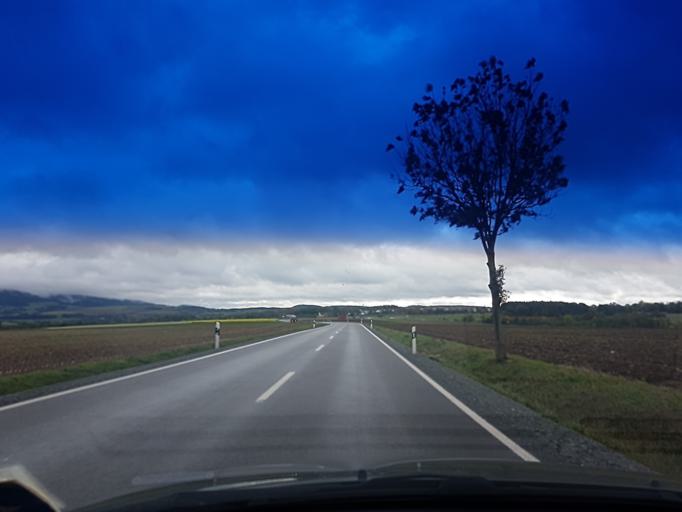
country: DE
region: Bavaria
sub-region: Upper Franconia
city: Bindlach
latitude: 50.0084
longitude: 11.6171
